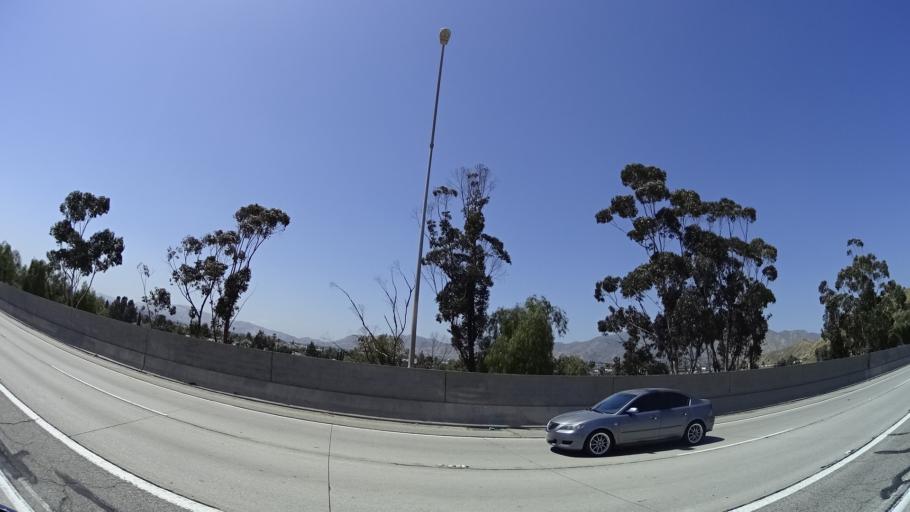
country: US
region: California
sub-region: Los Angeles County
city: San Fernando
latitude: 34.2862
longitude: -118.4110
